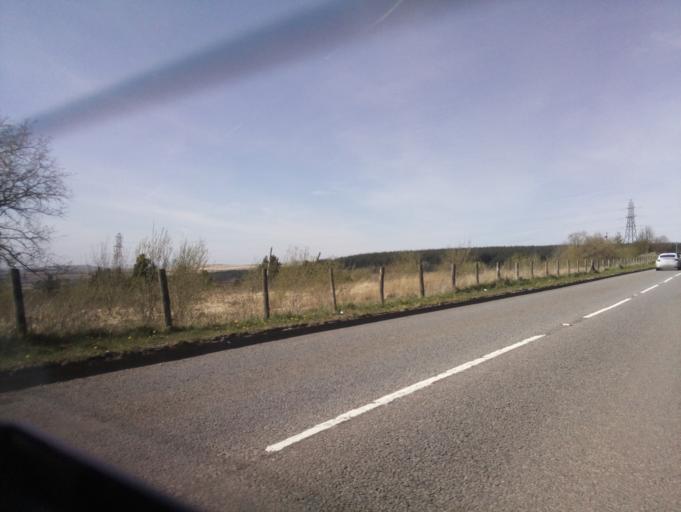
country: GB
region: Wales
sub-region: Rhondda Cynon Taf
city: Aberdare
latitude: 51.7492
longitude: -3.4424
